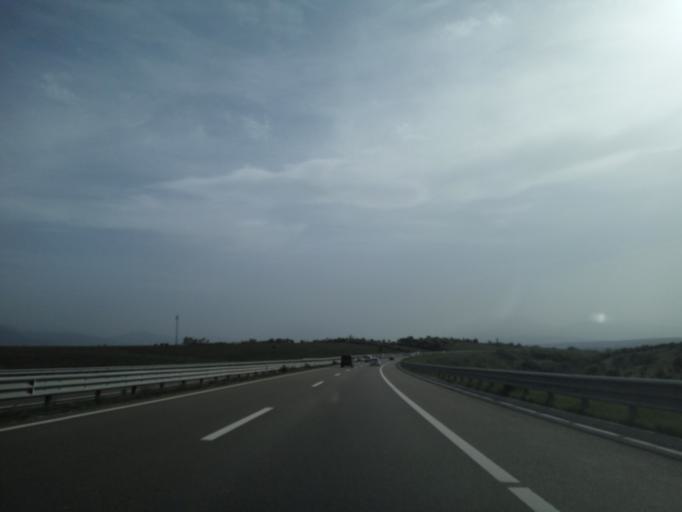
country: XK
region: Prizren
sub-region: Komuna e Therandes
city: Peqan
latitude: 42.3762
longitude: 20.8427
